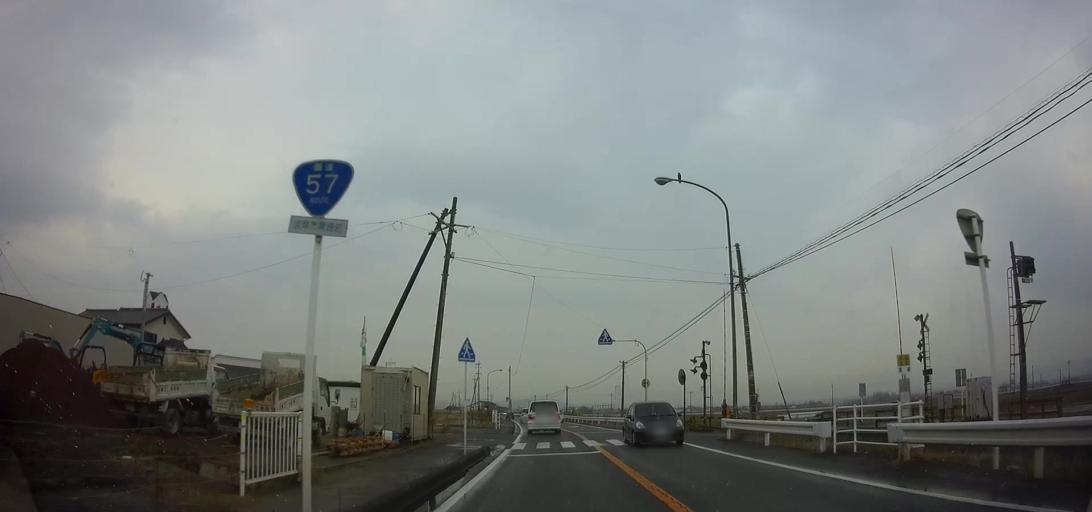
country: JP
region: Nagasaki
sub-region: Isahaya-shi
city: Isahaya
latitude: 32.8379
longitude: 130.1017
